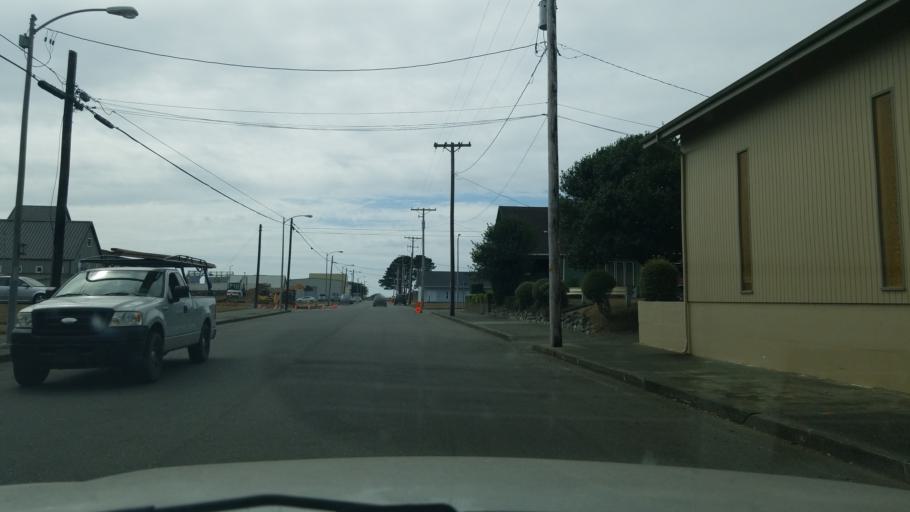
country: US
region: California
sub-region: Del Norte County
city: Crescent City
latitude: 41.7505
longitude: -124.1992
